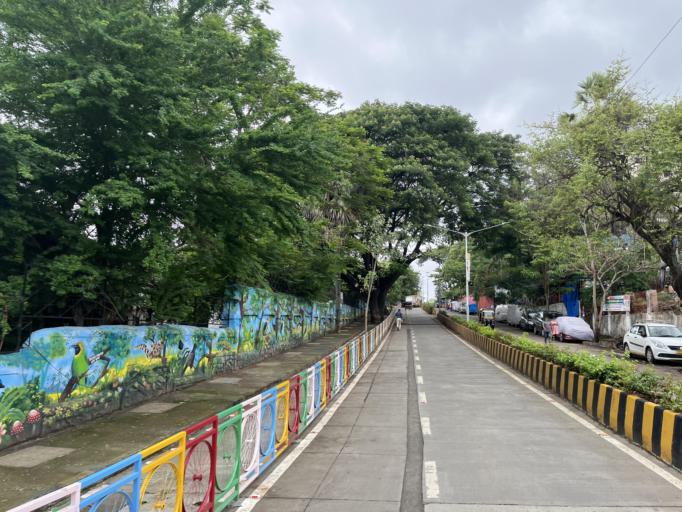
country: IN
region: Maharashtra
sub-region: Mumbai Suburban
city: Borivli
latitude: 19.2327
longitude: 72.8697
